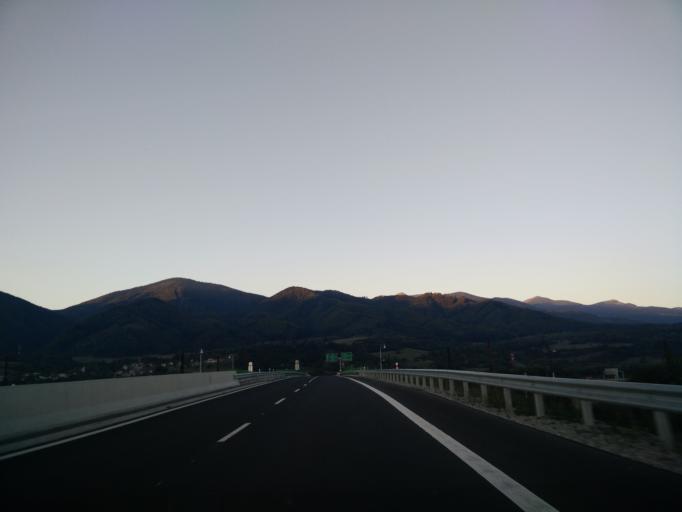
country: SK
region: Zilinsky
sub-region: Okres Zilina
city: Vrutky
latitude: 49.1064
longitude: 18.9568
